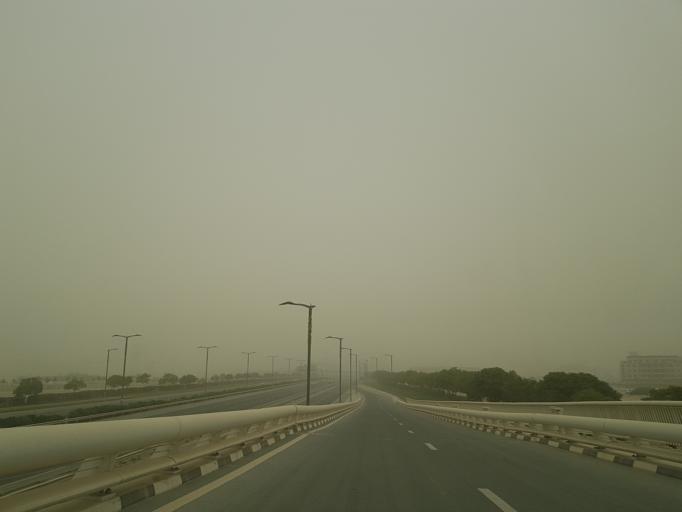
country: AE
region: Dubai
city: Dubai
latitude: 25.1616
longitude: 55.2975
